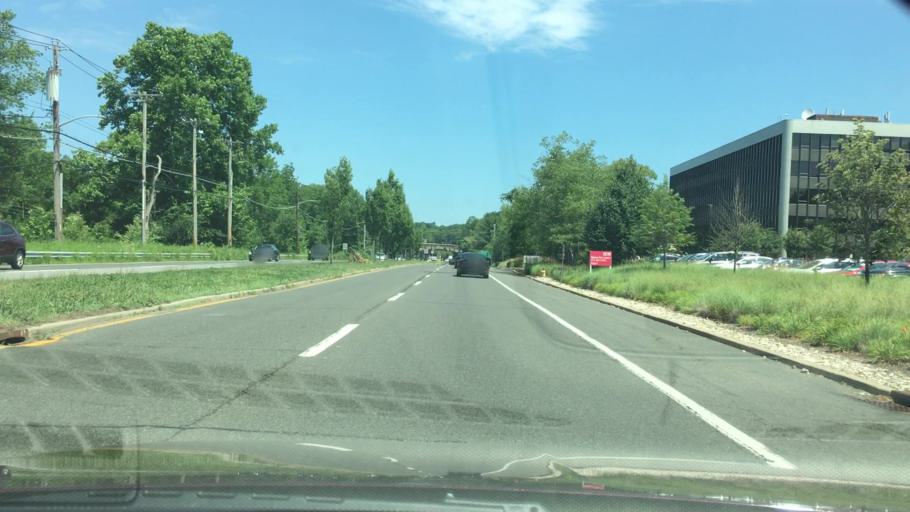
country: US
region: New York
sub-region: Westchester County
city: Harrison
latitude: 40.9798
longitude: -73.7435
